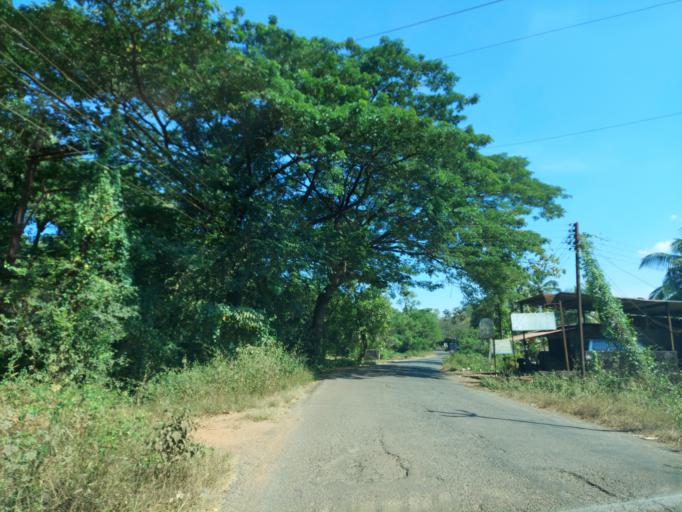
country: IN
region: Maharashtra
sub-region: Sindhudurg
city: Kudal
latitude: 15.9887
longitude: 73.6787
